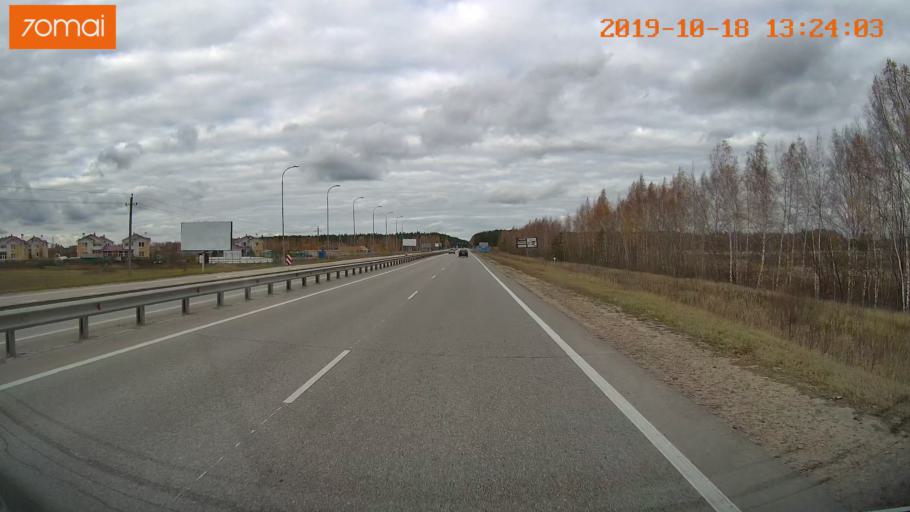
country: RU
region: Rjazan
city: Polyany
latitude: 54.7252
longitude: 39.8463
